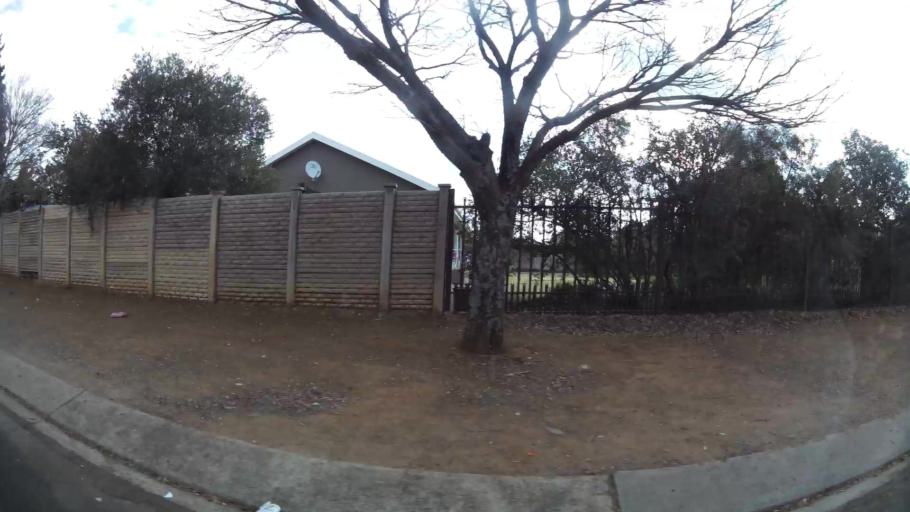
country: ZA
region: Orange Free State
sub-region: Mangaung Metropolitan Municipality
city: Bloemfontein
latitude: -29.0759
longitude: 26.2116
